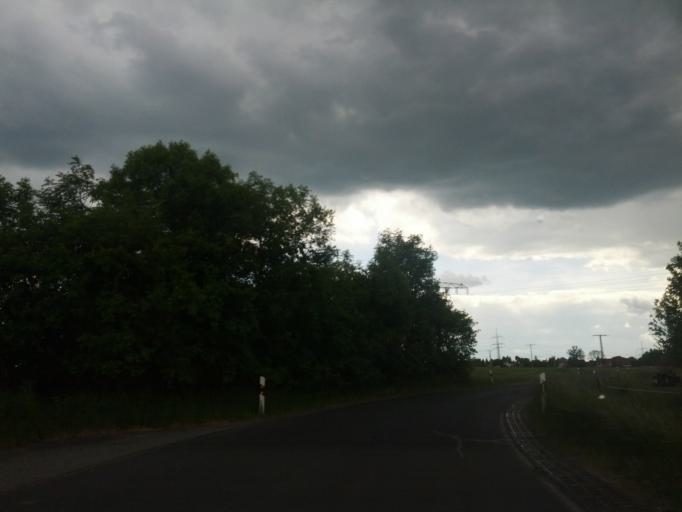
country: DE
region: Thuringia
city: Haina
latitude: 50.9808
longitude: 10.5216
